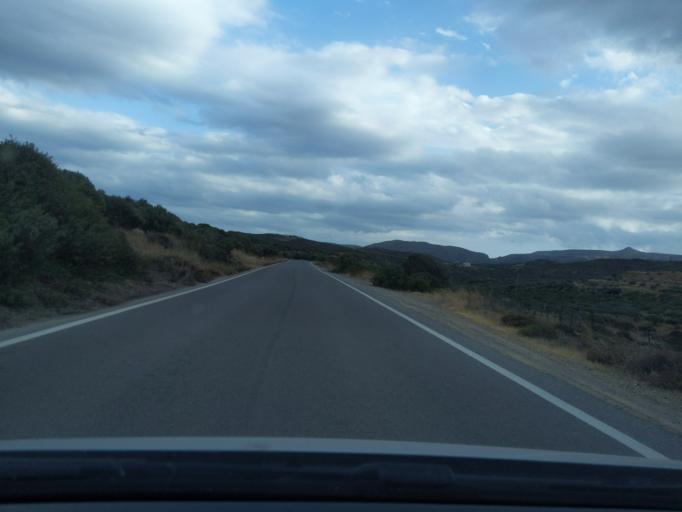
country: GR
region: Crete
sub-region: Nomos Lasithiou
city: Palekastro
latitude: 35.2301
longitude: 26.2540
